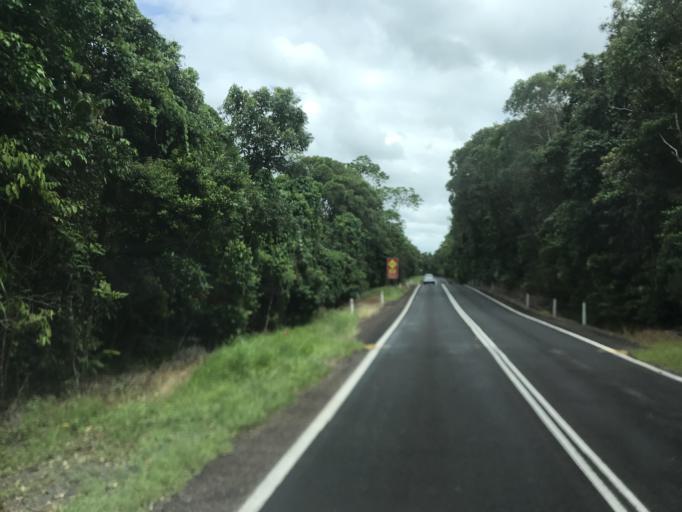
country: AU
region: Queensland
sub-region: Cassowary Coast
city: Innisfail
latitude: -17.8649
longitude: 146.0664
